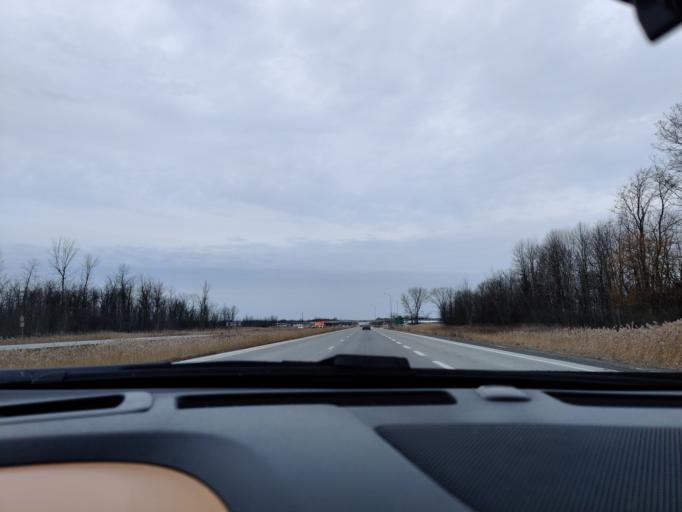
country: US
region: New York
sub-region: St. Lawrence County
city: Norfolk
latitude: 44.9198
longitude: -75.1912
